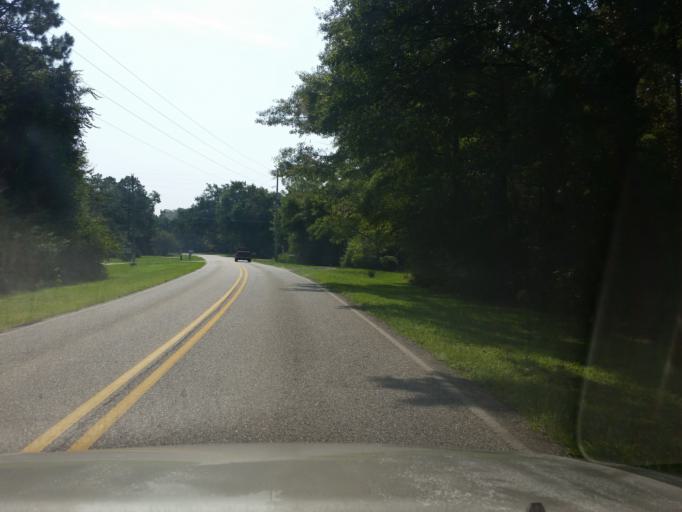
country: US
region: Alabama
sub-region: Baldwin County
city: Elberta
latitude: 30.5130
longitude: -87.4708
